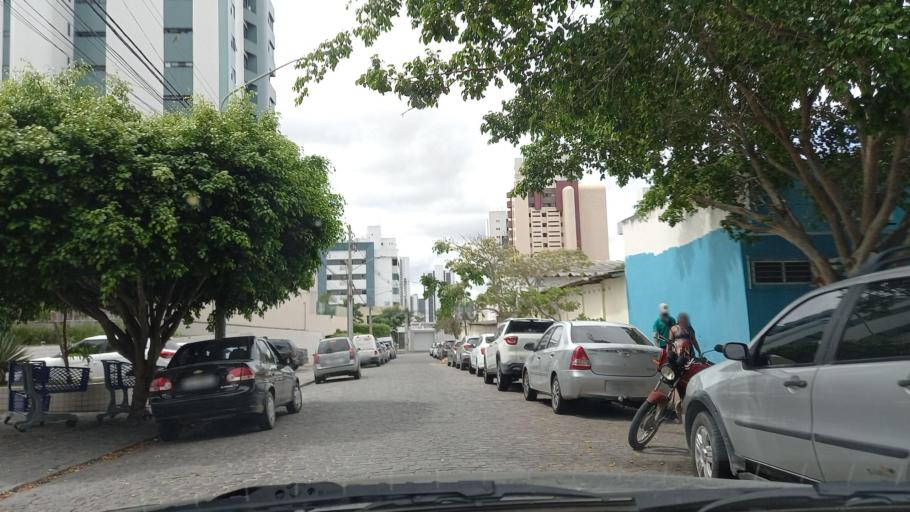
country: BR
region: Pernambuco
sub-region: Caruaru
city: Caruaru
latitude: -8.2698
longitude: -35.9744
